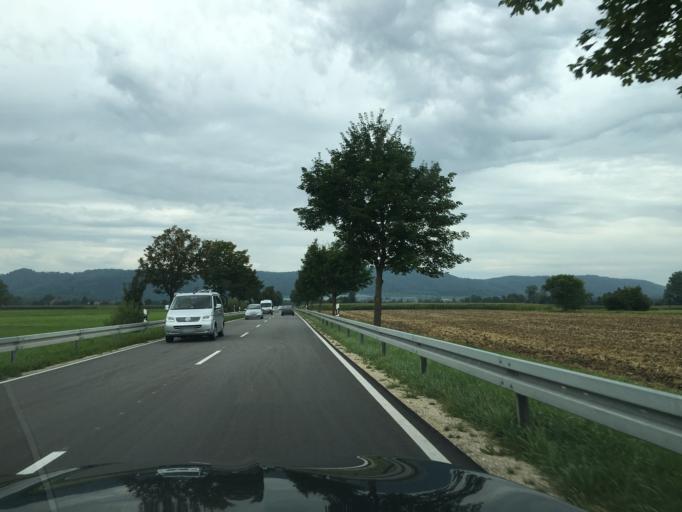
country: DE
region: Baden-Wuerttemberg
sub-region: Freiburg Region
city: Stockach
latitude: 47.8169
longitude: 9.0007
